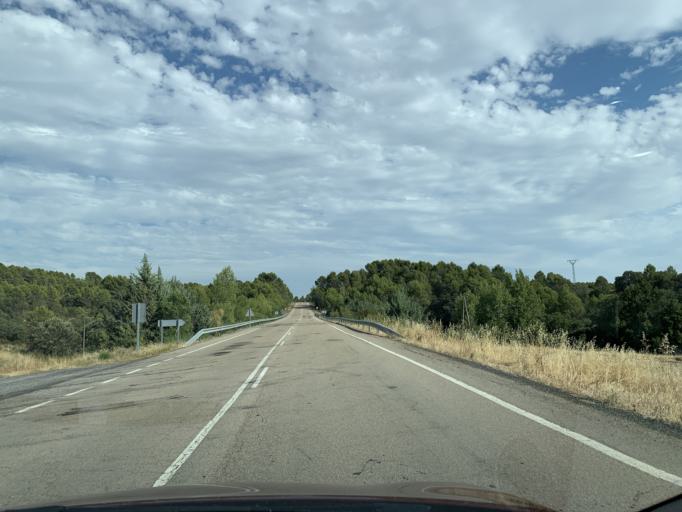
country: ES
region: Aragon
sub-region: Provincia de Zaragoza
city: Santa Eulalia de Gallego
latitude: 42.3052
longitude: -0.7440
